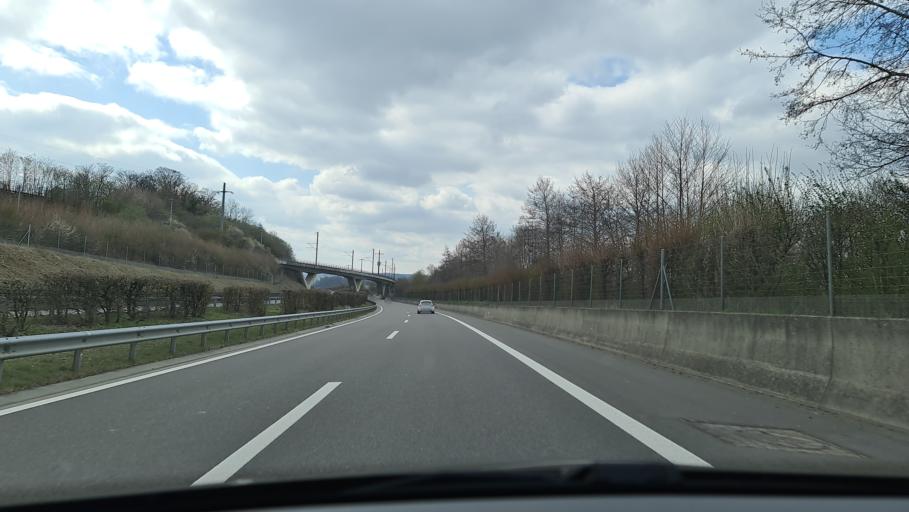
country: CH
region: Jura
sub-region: Porrentruy District
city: Alle
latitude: 47.4173
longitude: 7.1256
